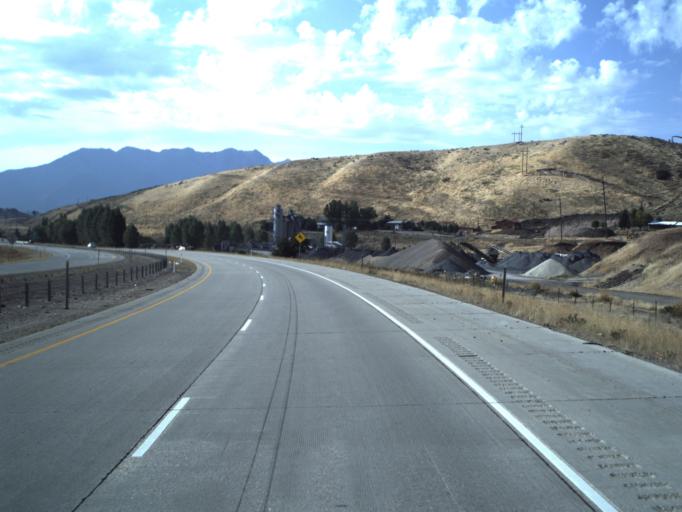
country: US
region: Utah
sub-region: Morgan County
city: Mountain Green
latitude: 41.1093
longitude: -111.7499
